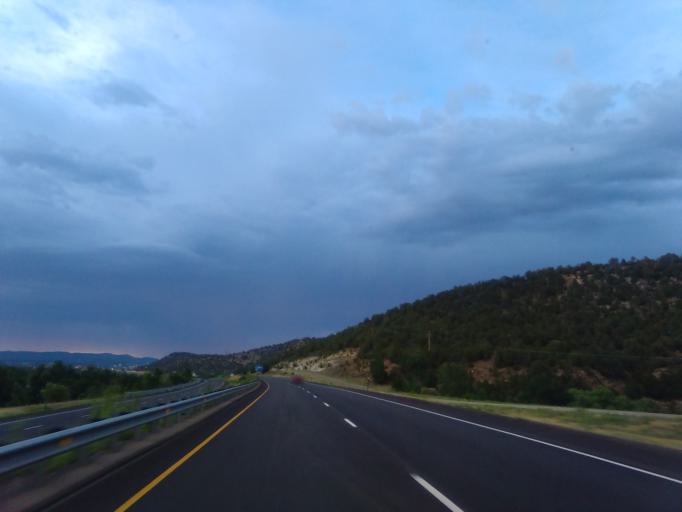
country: US
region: Colorado
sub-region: Las Animas County
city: Trinidad
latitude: 37.1109
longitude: -104.5221
